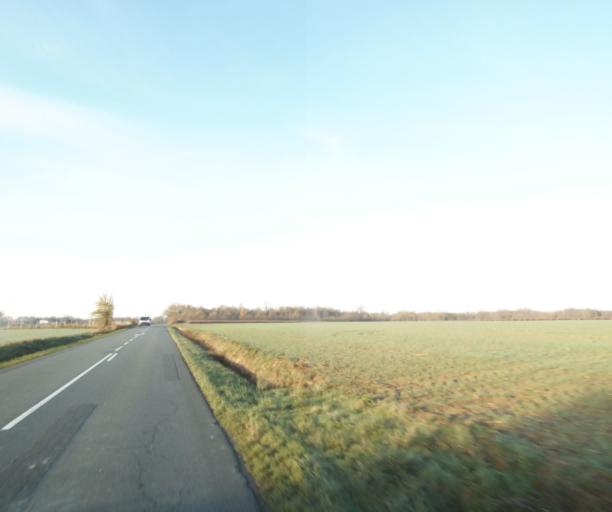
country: FR
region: Poitou-Charentes
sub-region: Departement de la Charente-Maritime
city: Fontcouverte
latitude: 45.7729
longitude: -0.5707
